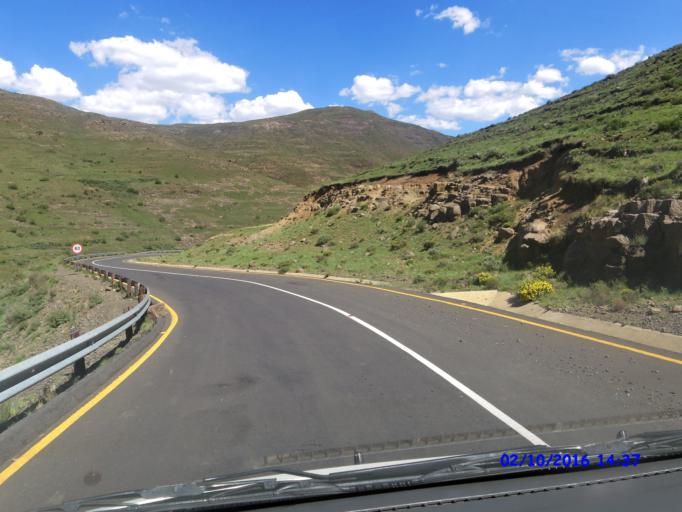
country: LS
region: Maseru
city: Nako
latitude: -29.5027
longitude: 28.0625
